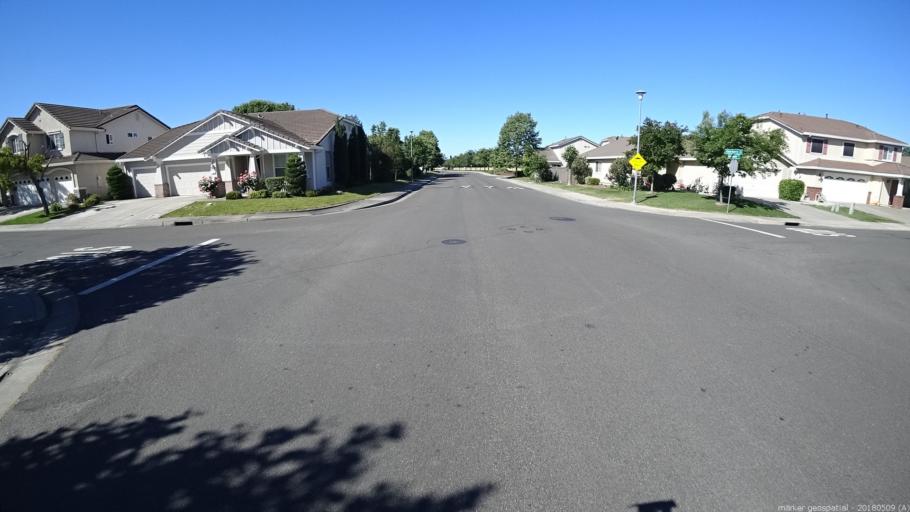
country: US
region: California
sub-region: Sacramento County
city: Elverta
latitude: 38.6687
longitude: -121.5222
